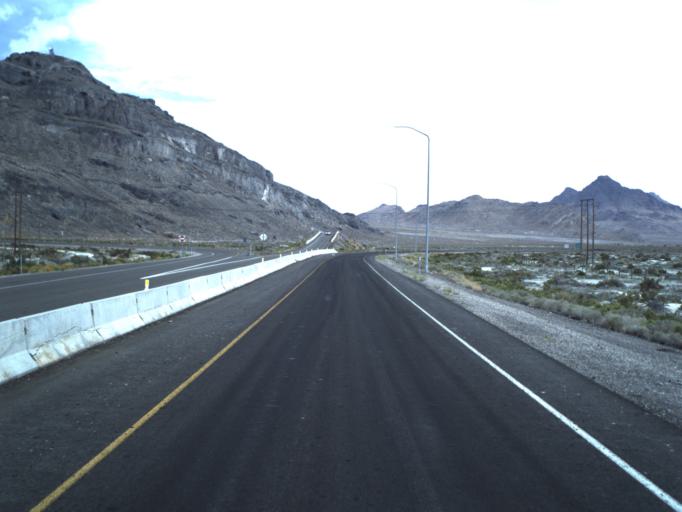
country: US
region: Utah
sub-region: Tooele County
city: Wendover
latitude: 40.7417
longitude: -114.0187
